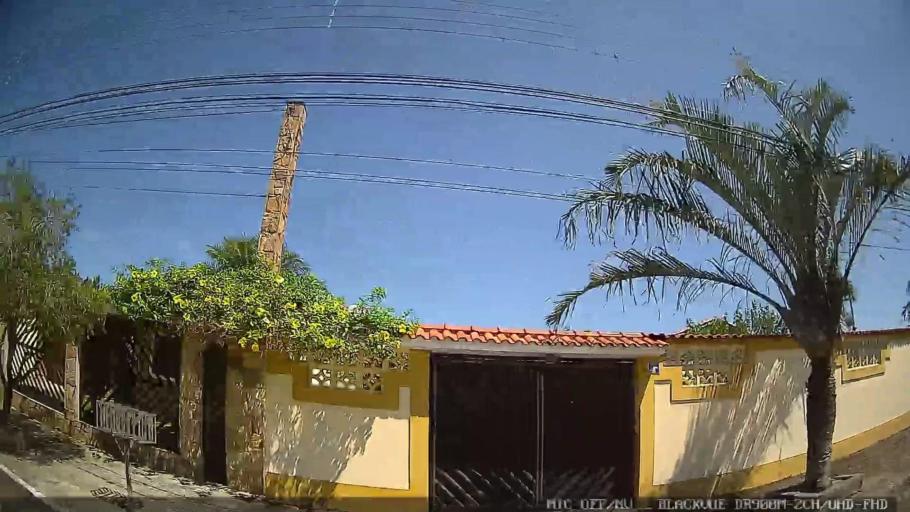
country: BR
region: Sao Paulo
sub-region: Peruibe
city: Peruibe
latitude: -24.2999
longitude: -46.9766
